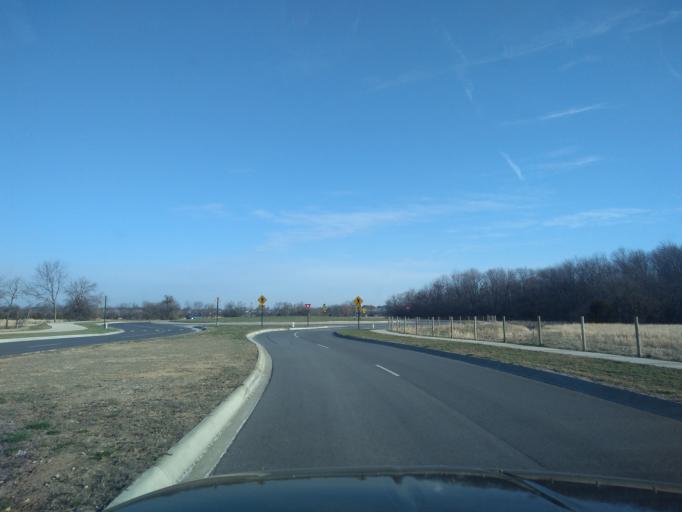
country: US
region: Arkansas
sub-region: Washington County
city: Farmington
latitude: 36.0634
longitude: -94.2203
